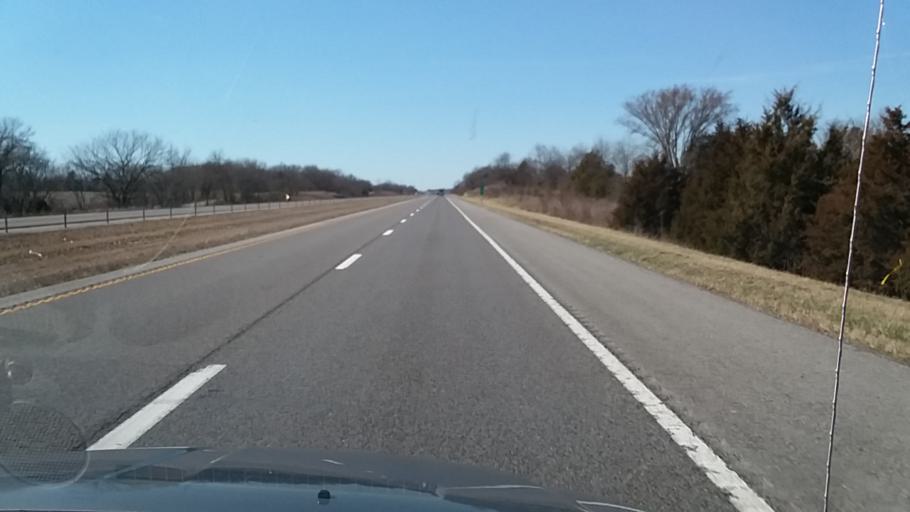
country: US
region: Missouri
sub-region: Perry County
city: Perryville
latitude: 37.6034
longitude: -89.7866
